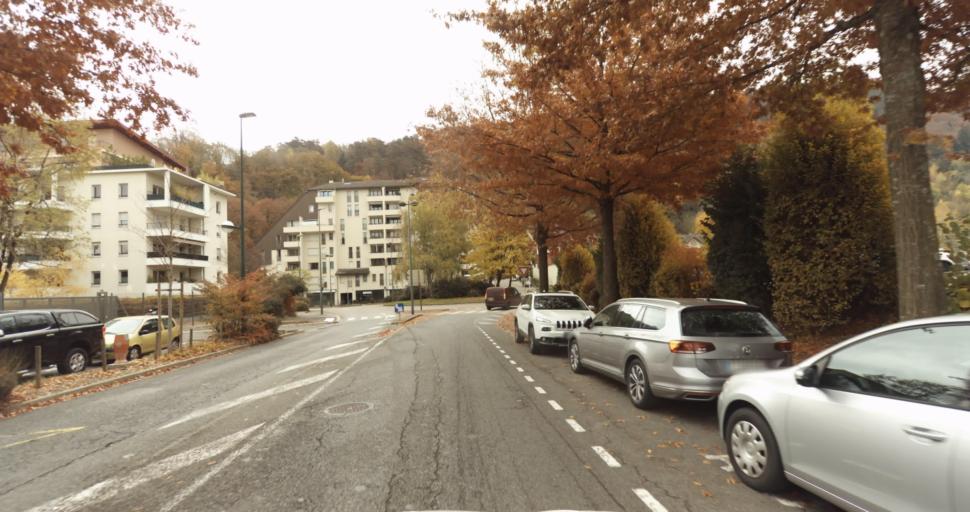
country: FR
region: Rhone-Alpes
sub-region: Departement de la Haute-Savoie
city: Annecy
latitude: 45.8905
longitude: 6.1226
